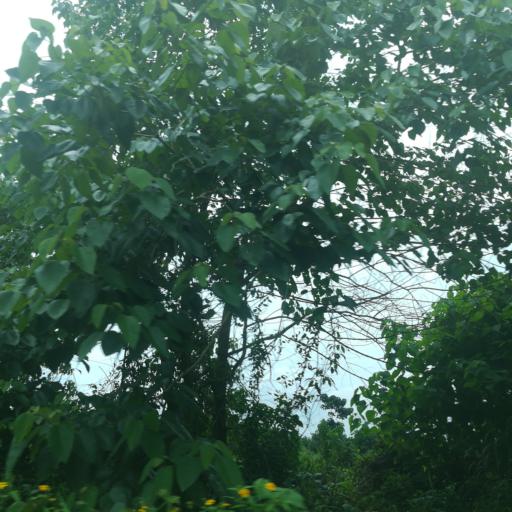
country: NG
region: Lagos
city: Ejirin
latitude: 6.6572
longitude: 3.7246
